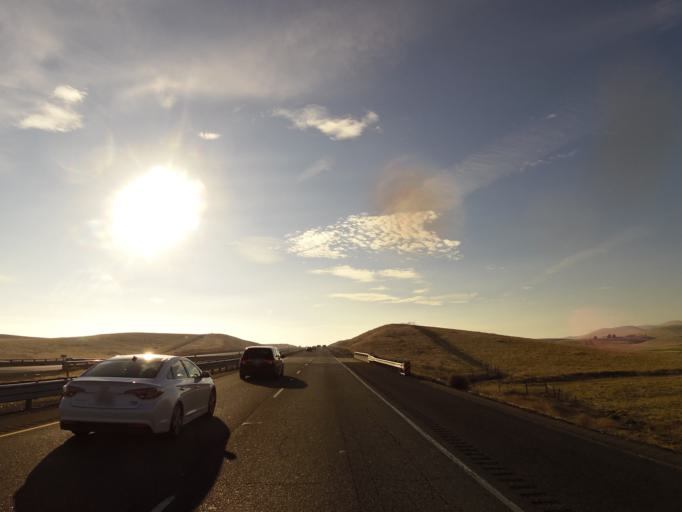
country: US
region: California
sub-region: Merced County
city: Gustine
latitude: 37.1780
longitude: -121.0639
